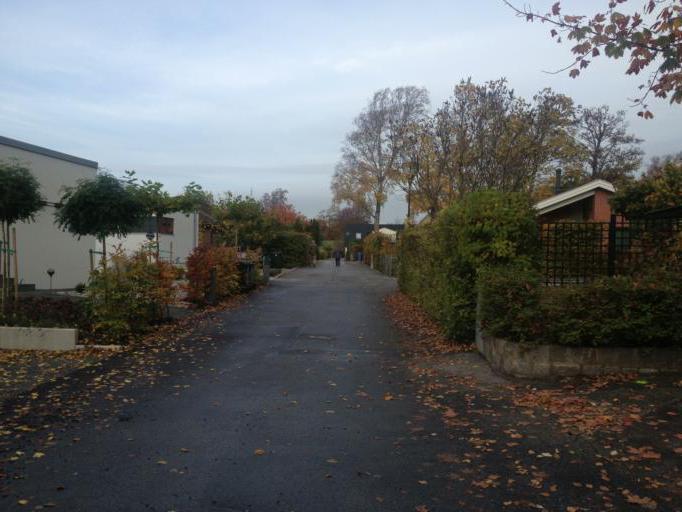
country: SE
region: Skane
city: Bjarred
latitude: 55.7171
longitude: 13.0160
